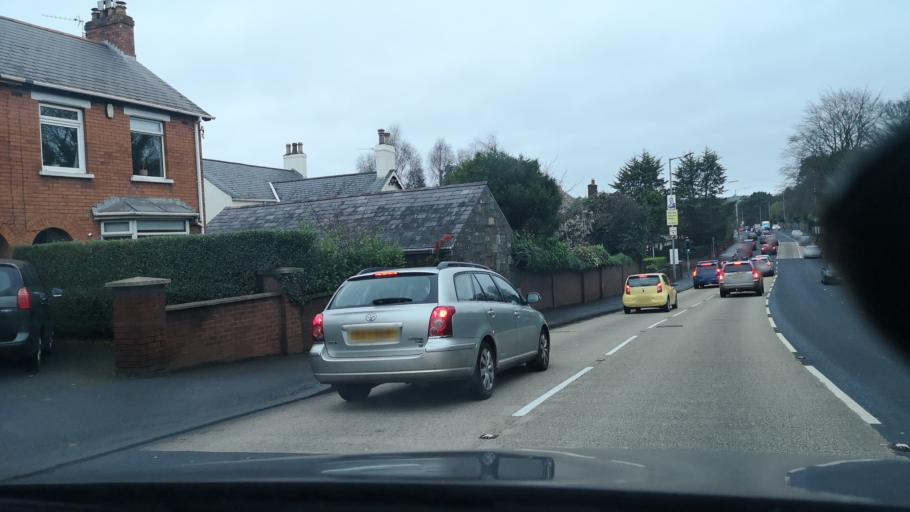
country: GB
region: Northern Ireland
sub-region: Castlereagh District
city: Castlereagh
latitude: 54.5859
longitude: -5.8611
